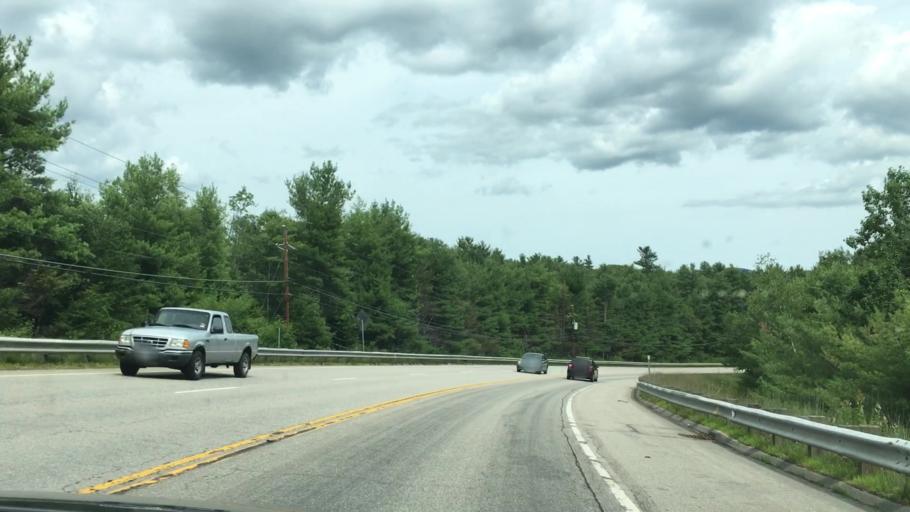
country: US
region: New Hampshire
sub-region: Hillsborough County
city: Peterborough
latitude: 42.8385
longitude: -71.9839
